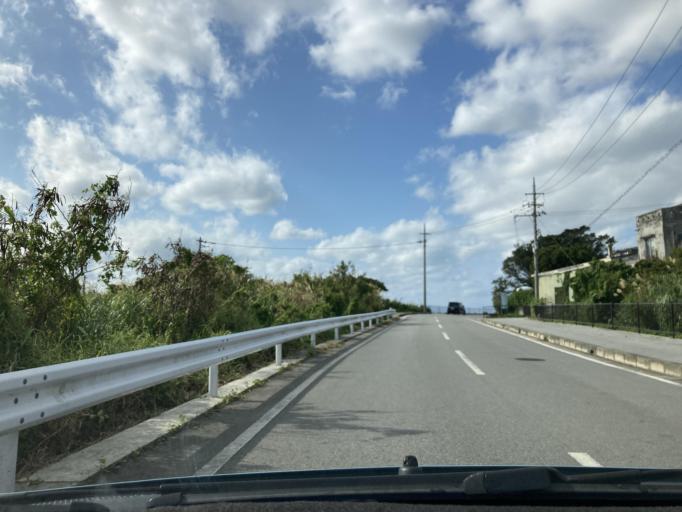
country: JP
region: Okinawa
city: Tomigusuku
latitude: 26.1708
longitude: 127.7607
